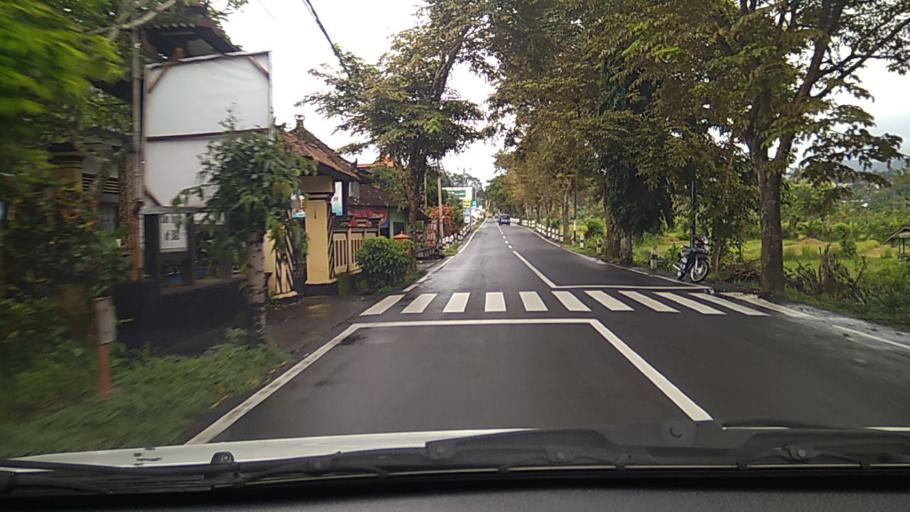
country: ID
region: Bali
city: Banjar Budakeling
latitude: -8.4294
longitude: 115.5919
